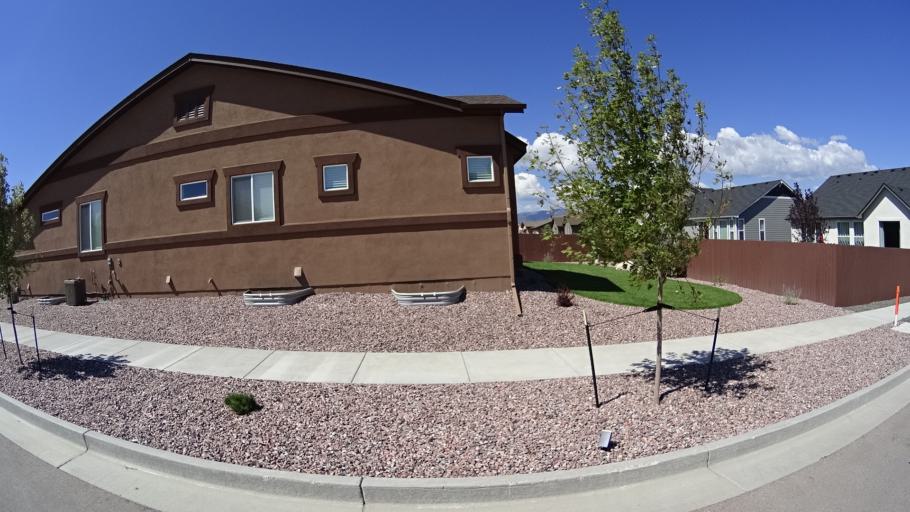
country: US
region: Colorado
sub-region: El Paso County
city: Black Forest
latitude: 38.9935
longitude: -104.7639
